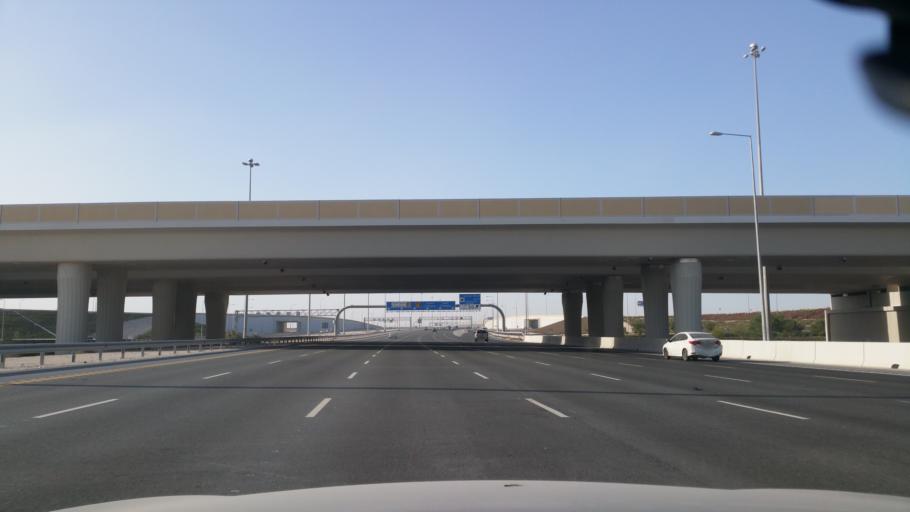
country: QA
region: Al Wakrah
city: Al Wukayr
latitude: 25.1832
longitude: 51.5487
